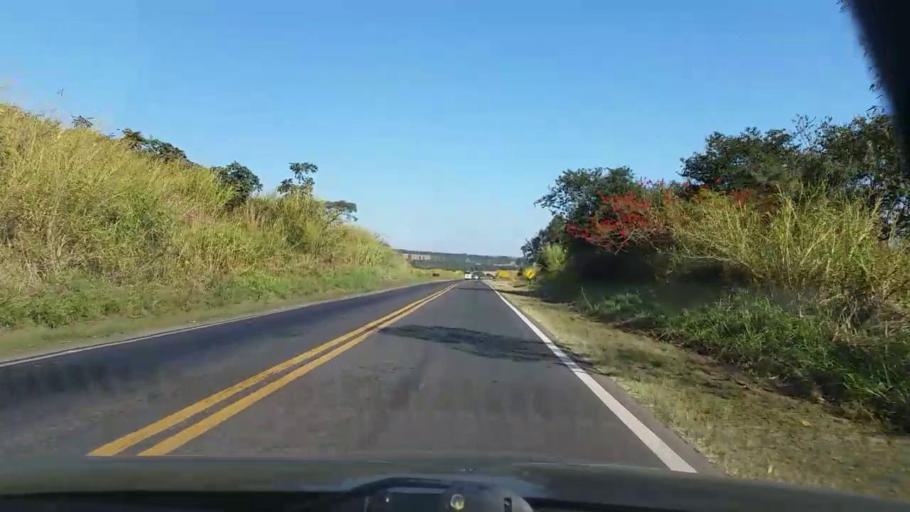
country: BR
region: Sao Paulo
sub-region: Itatinga
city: Itatinga
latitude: -22.9036
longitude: -48.7672
